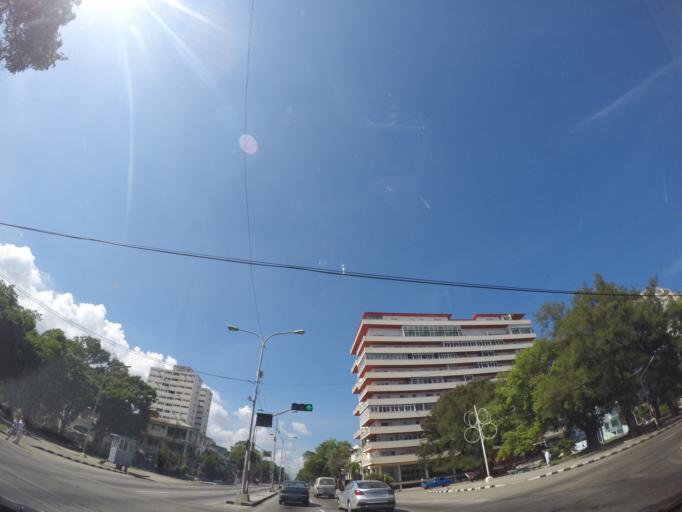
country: CU
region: La Habana
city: Regla
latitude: 23.1002
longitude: -82.3199
